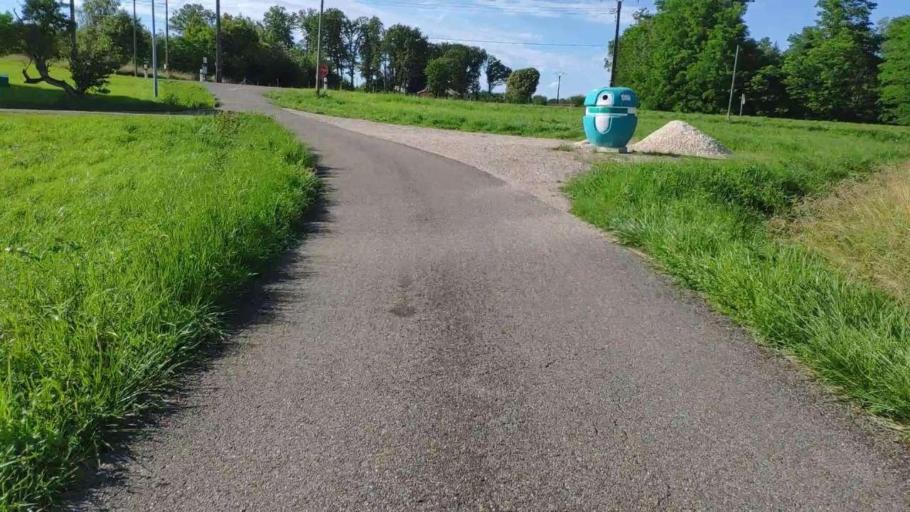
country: FR
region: Franche-Comte
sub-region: Departement du Jura
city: Bletterans
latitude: 46.8260
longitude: 5.5016
